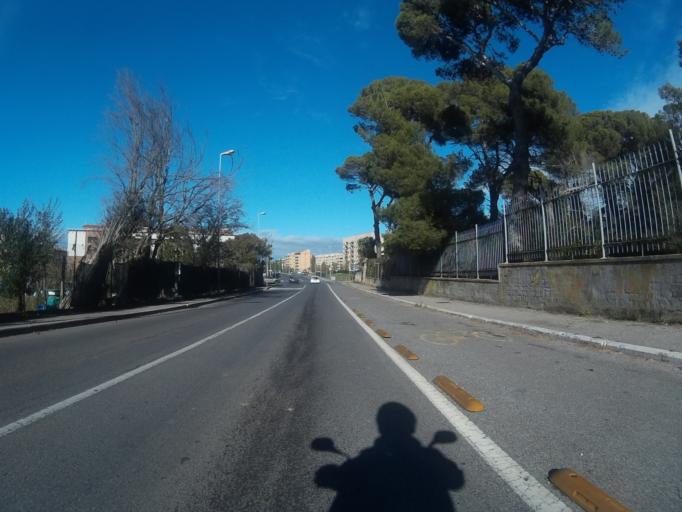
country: IT
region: Tuscany
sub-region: Provincia di Livorno
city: Livorno
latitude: 43.5240
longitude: 10.3461
